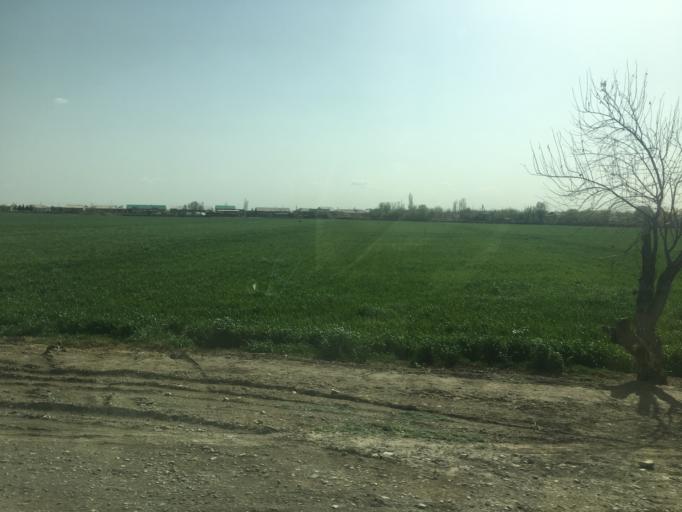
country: TM
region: Lebap
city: Farap
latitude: 39.2059
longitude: 63.5573
